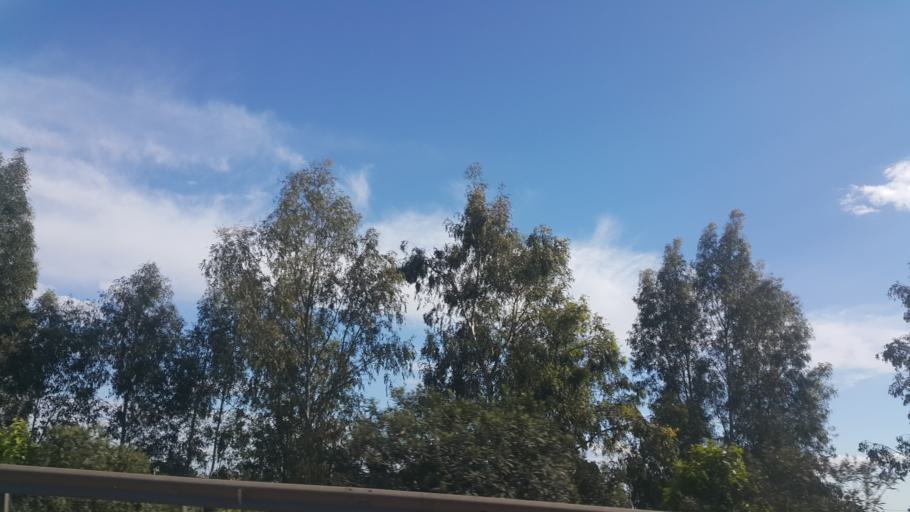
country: TR
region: Adana
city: Adana
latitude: 37.0250
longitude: 35.3606
